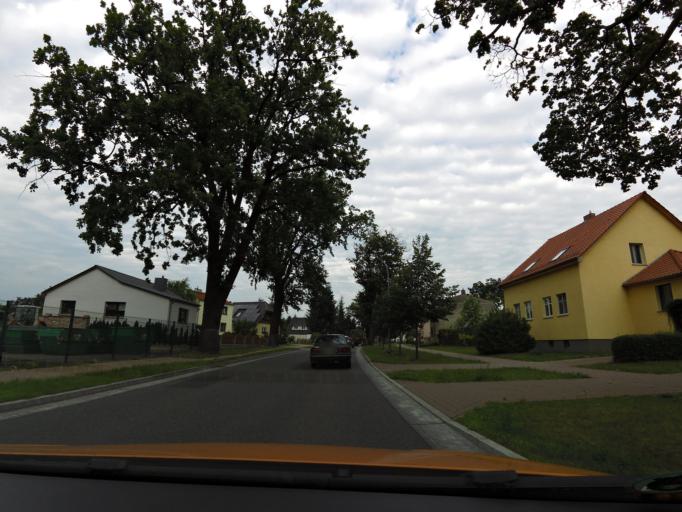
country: DE
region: Brandenburg
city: Roskow
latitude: 52.4099
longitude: 12.6903
